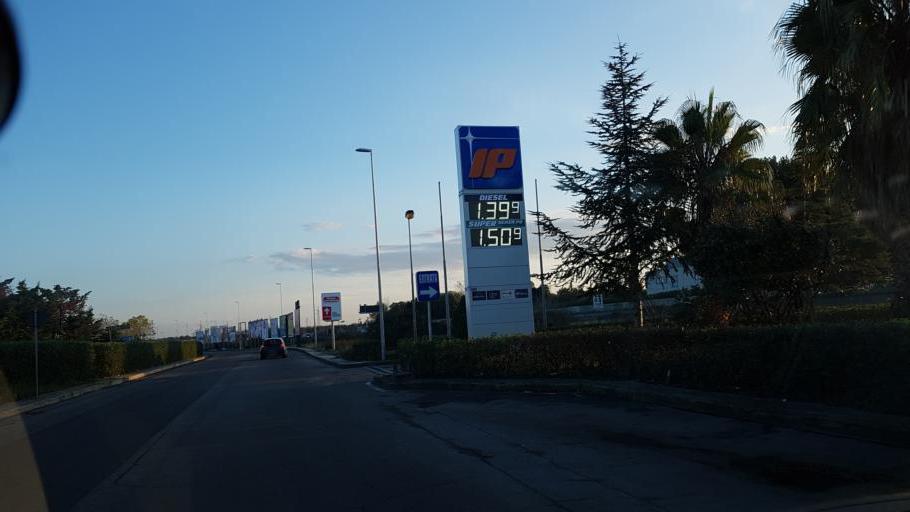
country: IT
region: Apulia
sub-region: Provincia di Lecce
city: Giorgilorio
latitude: 40.3760
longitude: 18.1418
